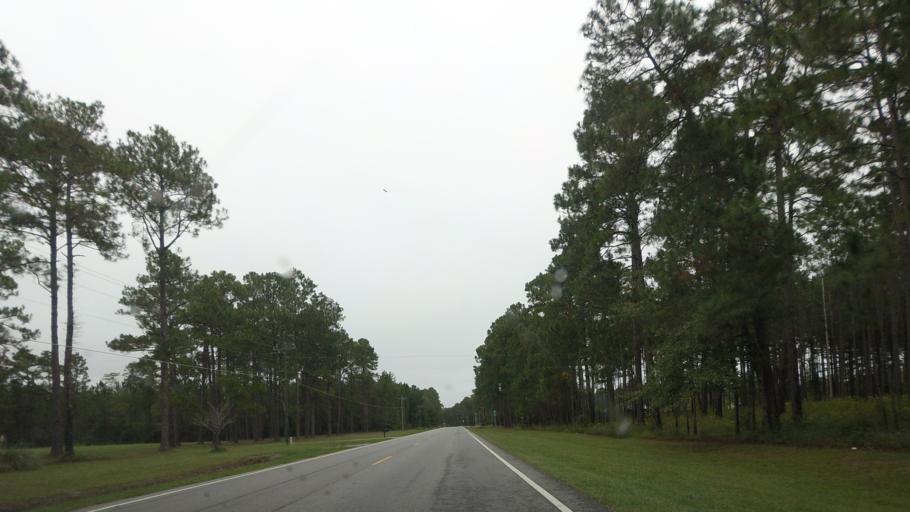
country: US
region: Georgia
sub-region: Berrien County
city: Nashville
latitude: 31.2498
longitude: -83.2415
